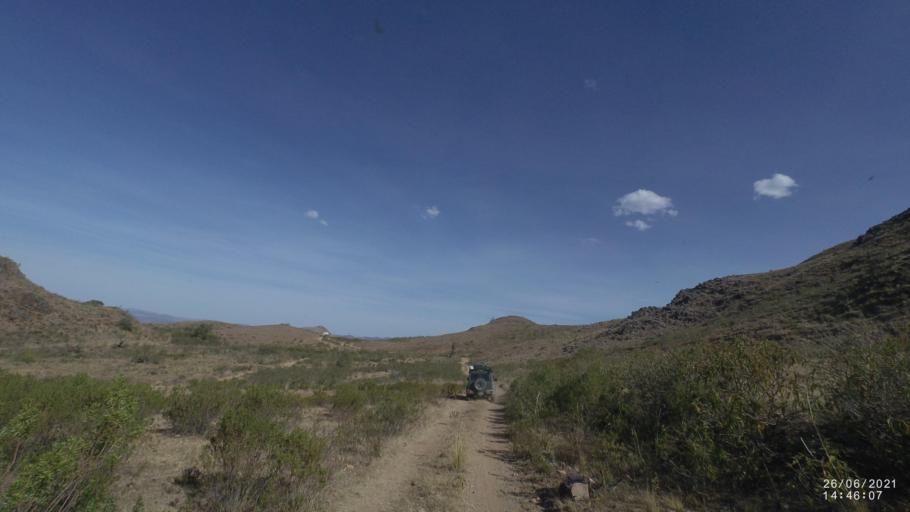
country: BO
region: Cochabamba
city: Mizque
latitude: -17.9155
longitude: -65.6259
